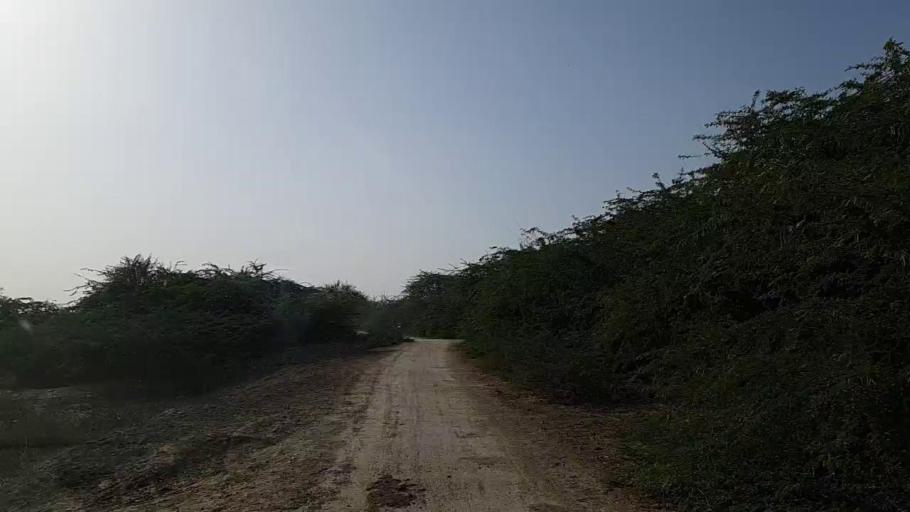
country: PK
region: Sindh
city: Jati
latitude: 24.2882
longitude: 68.2090
